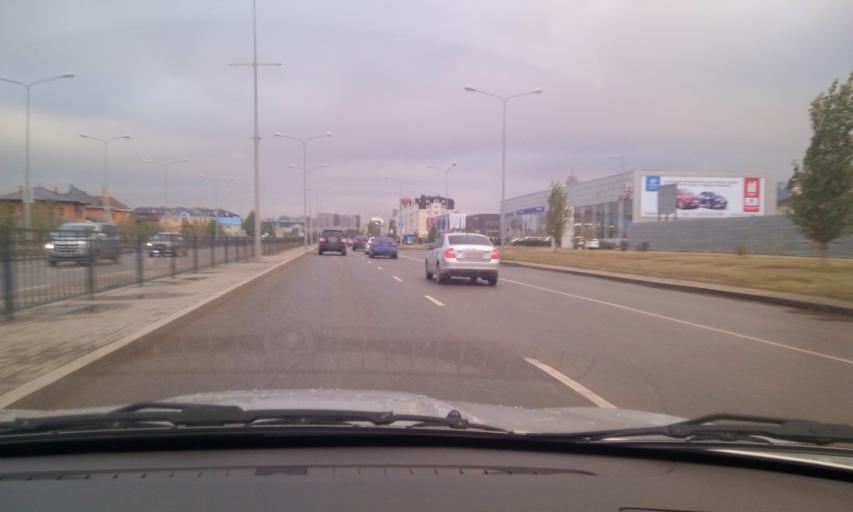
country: KZ
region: Astana Qalasy
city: Astana
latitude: 51.1471
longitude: 71.3981
